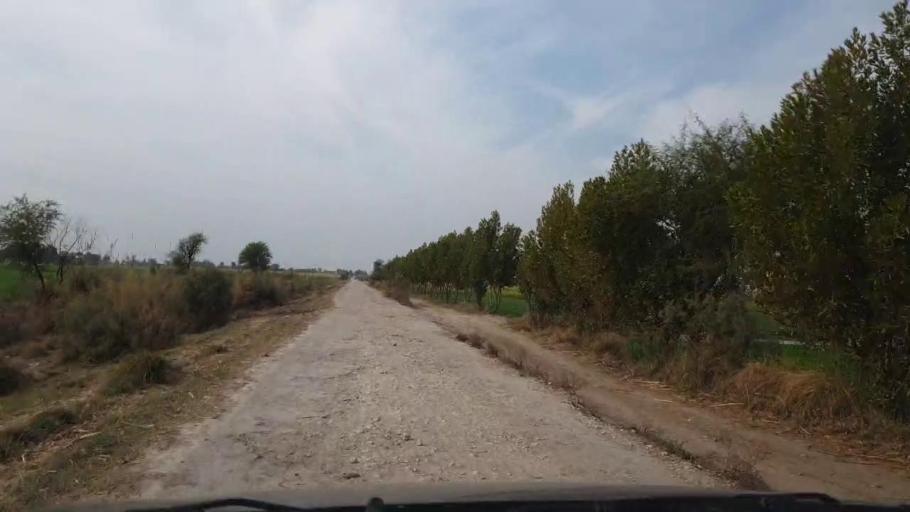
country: PK
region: Sindh
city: Sinjhoro
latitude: 26.0828
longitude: 68.8273
